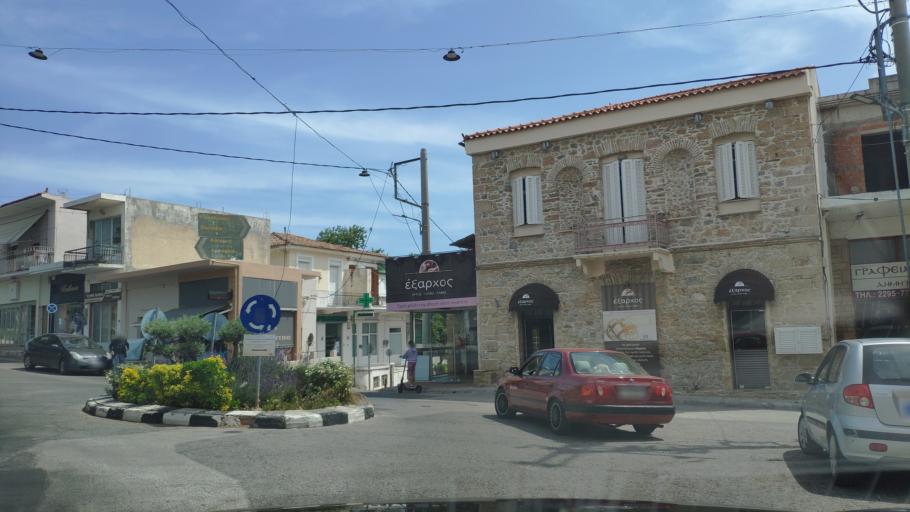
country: GR
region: Attica
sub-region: Nomarchia Anatolikis Attikis
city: Kapandriti
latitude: 38.2157
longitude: 23.8770
